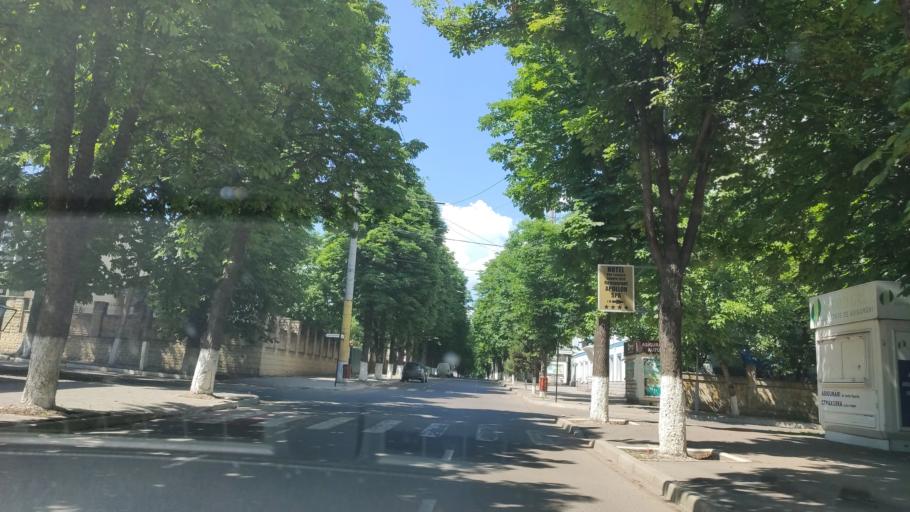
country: MD
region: Raionul Soroca
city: Soroca
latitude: 48.1513
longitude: 28.3022
